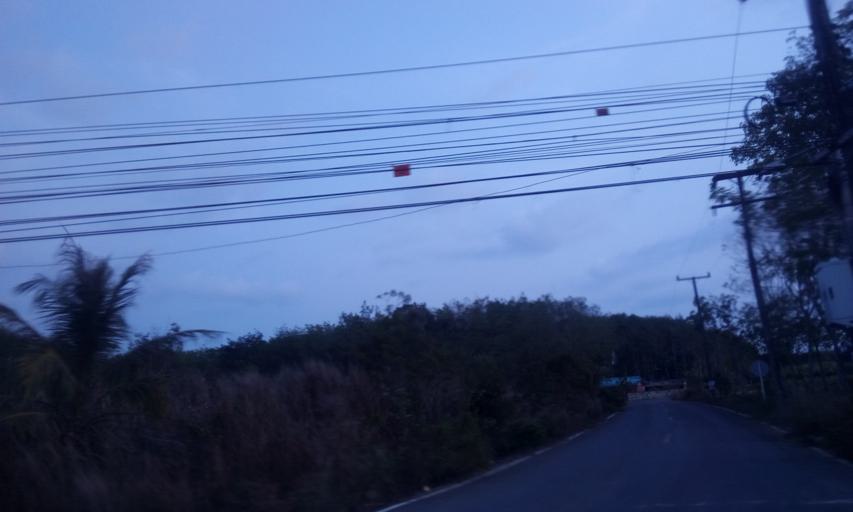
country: TH
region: Trat
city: Khao Saming
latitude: 12.2998
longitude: 102.3409
